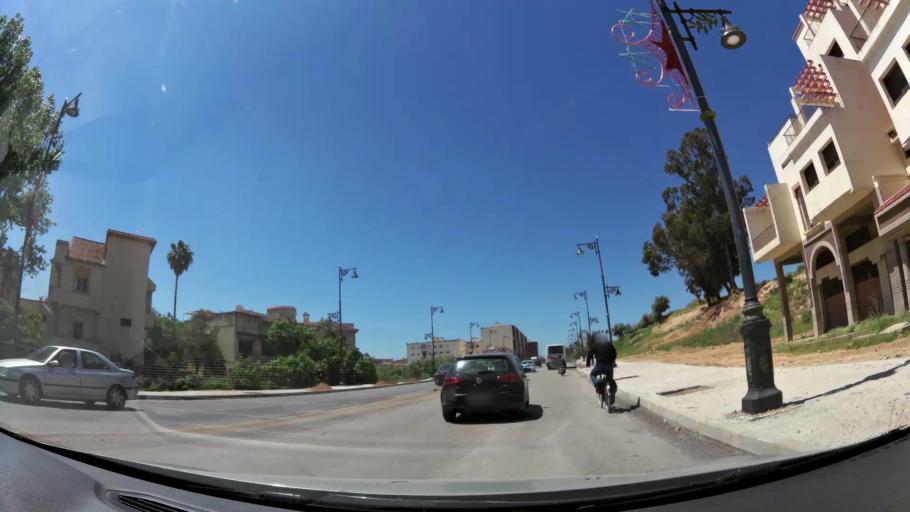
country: MA
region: Meknes-Tafilalet
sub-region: Meknes
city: Meknes
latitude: 33.8736
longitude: -5.5360
